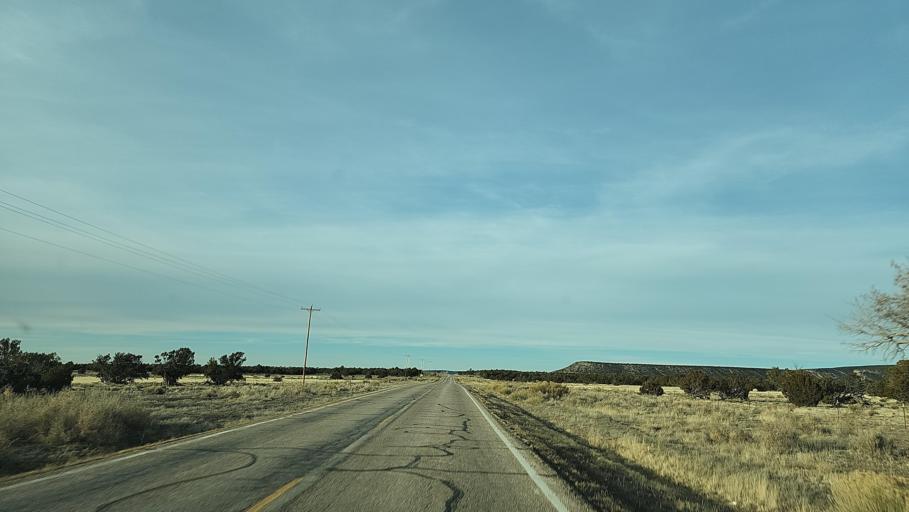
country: US
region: New Mexico
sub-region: McKinley County
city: Black Rock
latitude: 34.4434
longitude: -108.4270
